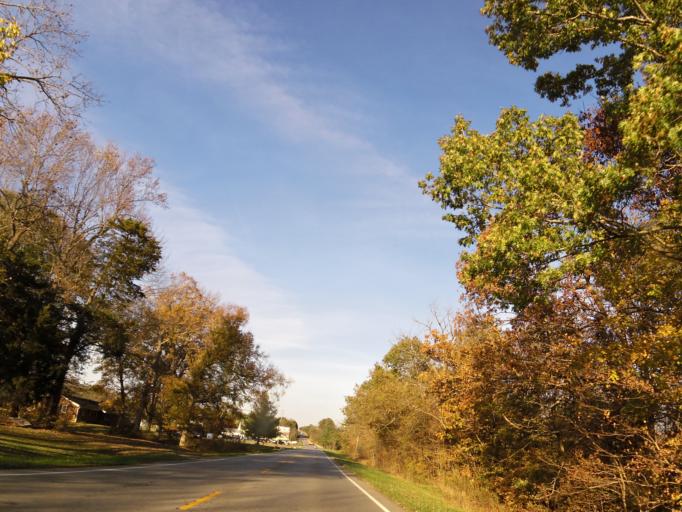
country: US
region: Kentucky
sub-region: Lincoln County
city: Stanford
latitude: 37.5667
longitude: -84.6201
